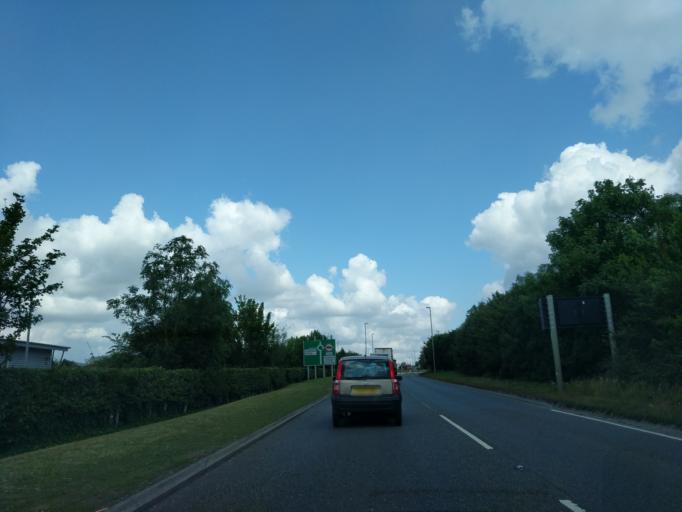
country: GB
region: England
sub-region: Suffolk
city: Exning
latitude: 52.2896
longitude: 0.3920
